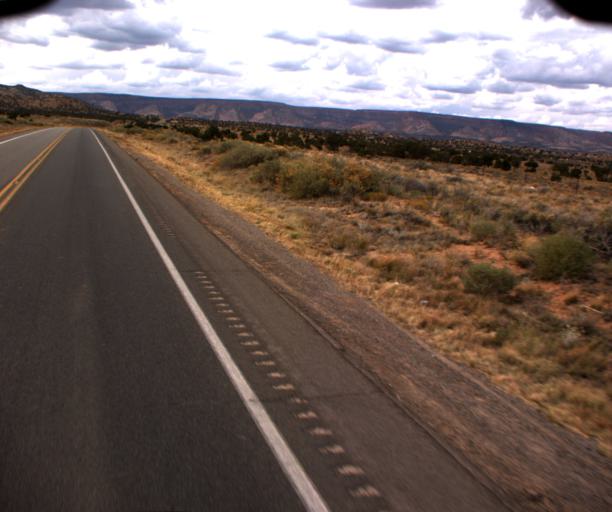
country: US
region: Arizona
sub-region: Navajo County
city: Kayenta
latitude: 36.7001
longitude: -110.2976
